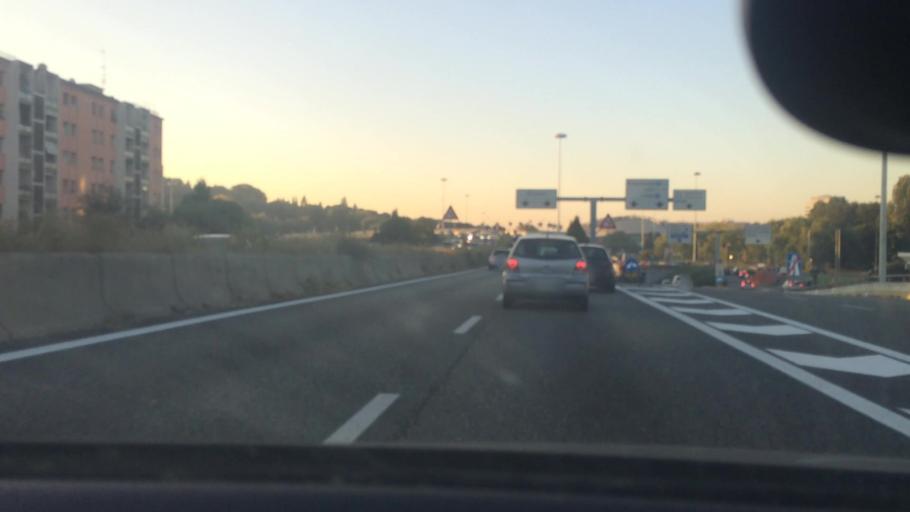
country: IT
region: Lombardy
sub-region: Citta metropolitana di Milano
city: Baranzate
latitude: 45.4973
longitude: 9.1303
